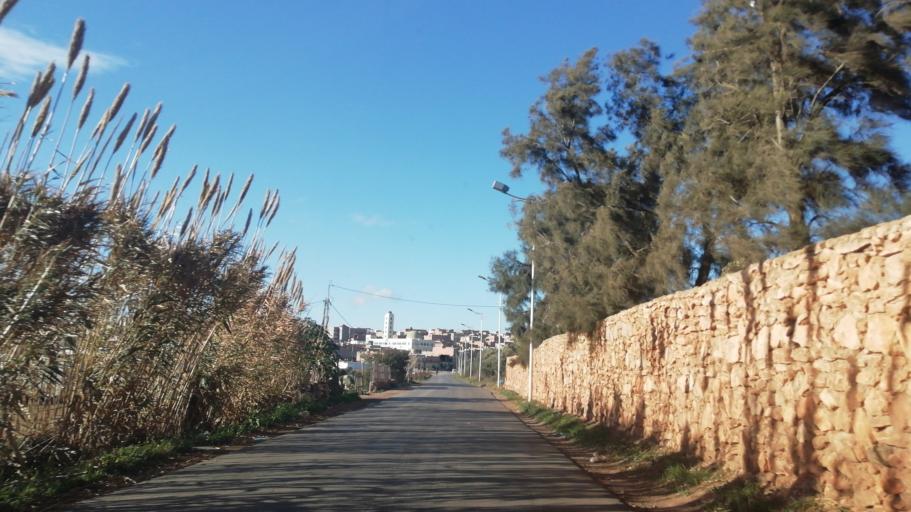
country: DZ
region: Oran
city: Sidi ech Chahmi
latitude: 35.6864
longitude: -0.4951
